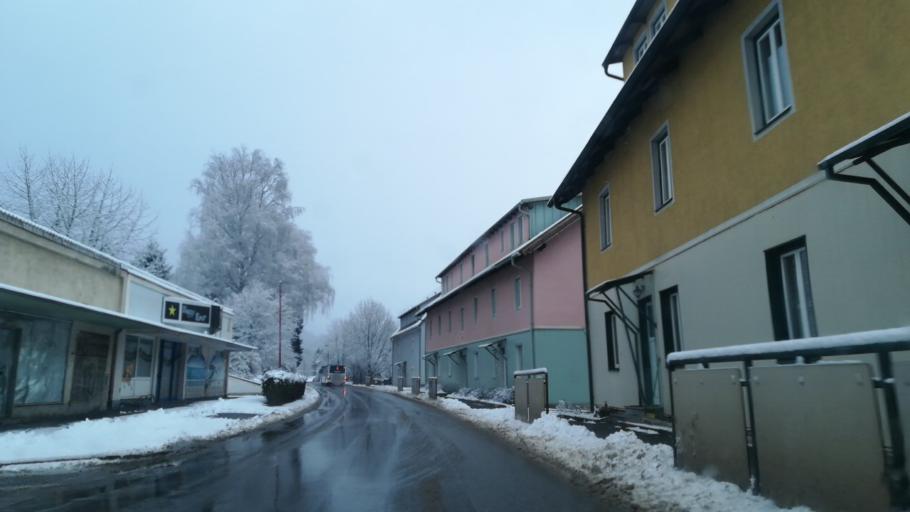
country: AT
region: Styria
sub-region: Politischer Bezirk Murtal
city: Fohnsdorf
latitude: 47.2061
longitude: 14.6697
